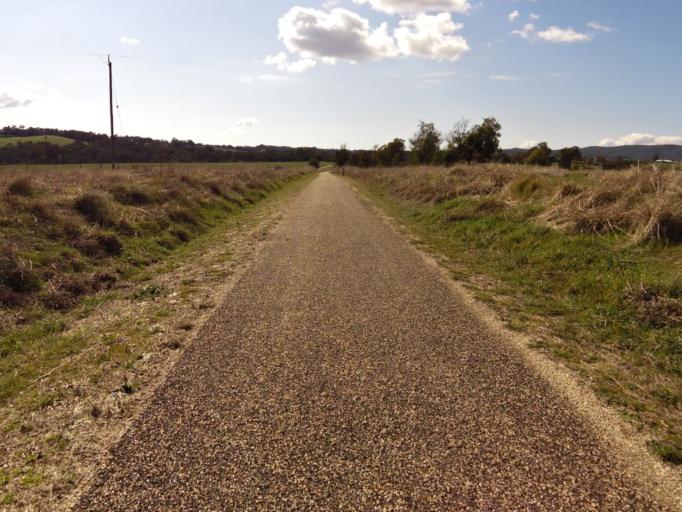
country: AU
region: Victoria
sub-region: Wangaratta
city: Wangaratta
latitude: -36.3975
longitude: 146.6517
